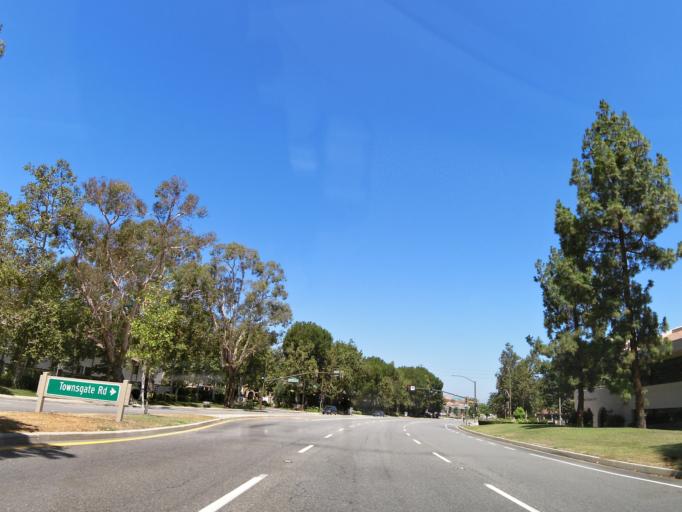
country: US
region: California
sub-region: Ventura County
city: Thousand Oaks
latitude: 34.1601
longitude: -118.8373
